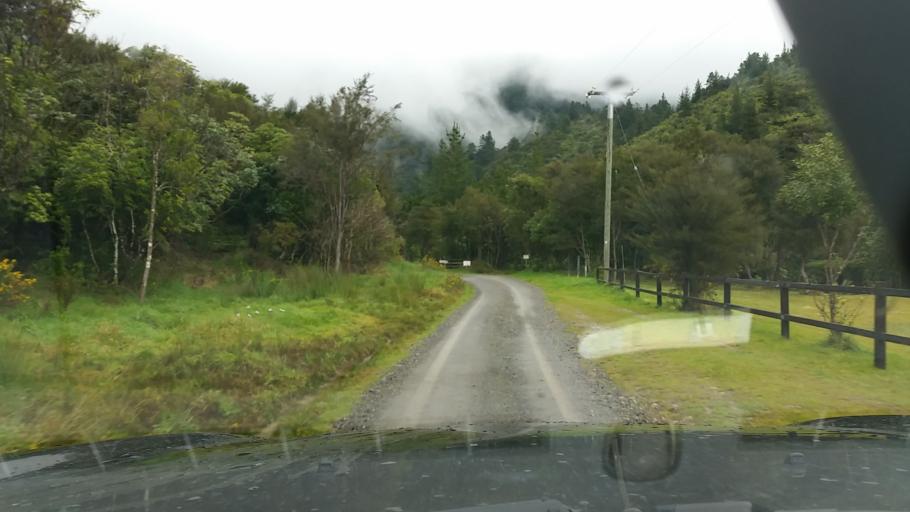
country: NZ
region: Marlborough
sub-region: Marlborough District
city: Picton
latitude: -41.2912
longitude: 174.0403
